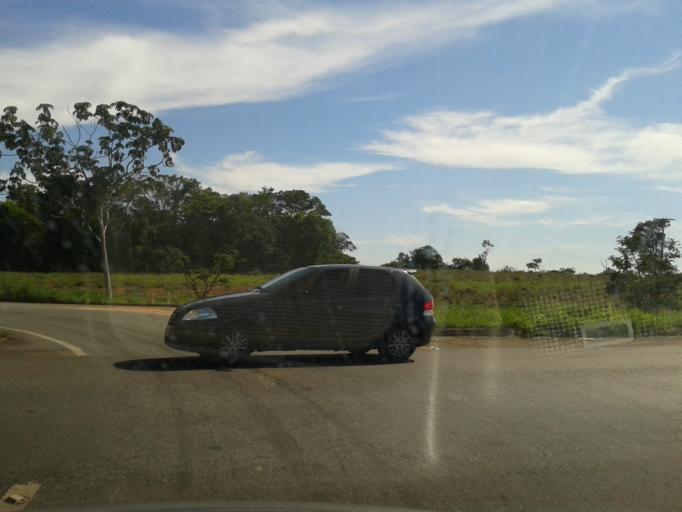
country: BR
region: Goias
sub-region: Piracanjuba
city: Piracanjuba
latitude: -17.2313
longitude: -48.7114
